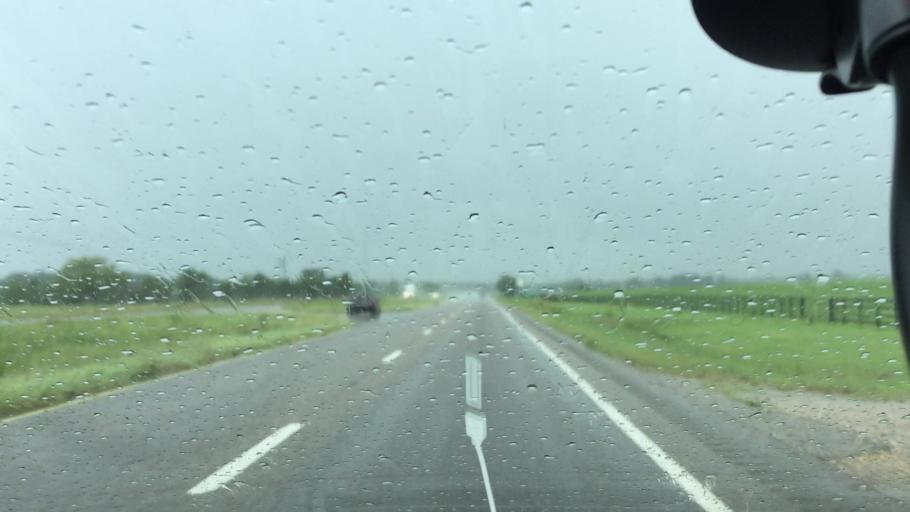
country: US
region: Alabama
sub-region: Montgomery County
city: Pike Road
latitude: 32.2363
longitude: -86.1272
